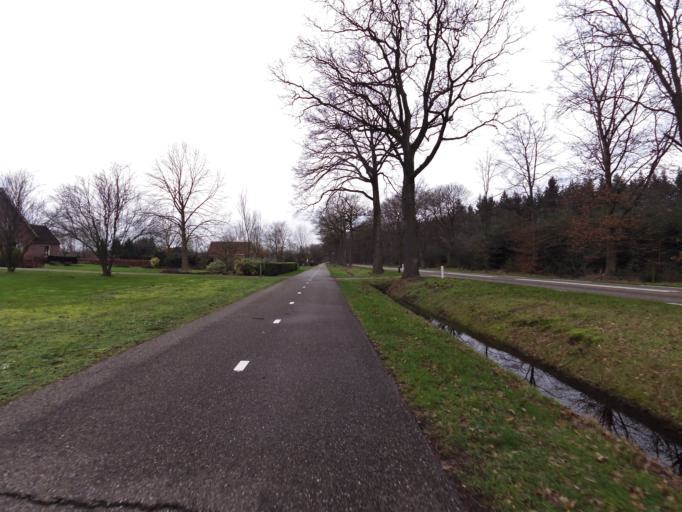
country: NL
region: Gelderland
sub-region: Oude IJsselstreek
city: Wisch
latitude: 51.9534
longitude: 6.3849
